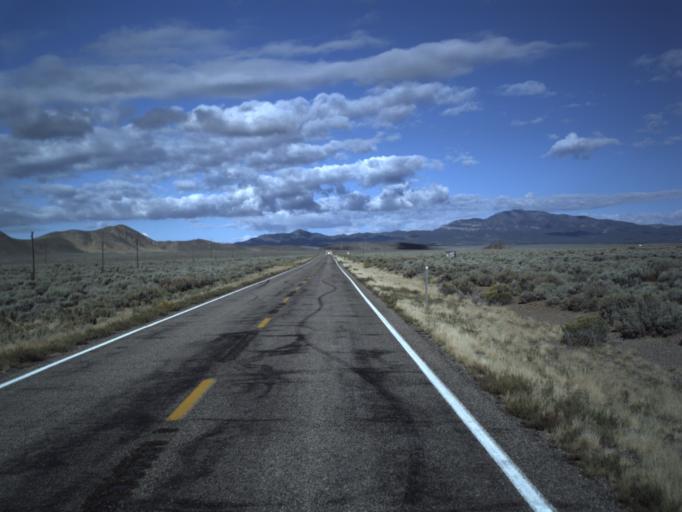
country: US
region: Utah
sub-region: Beaver County
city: Milford
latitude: 38.4112
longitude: -113.0667
